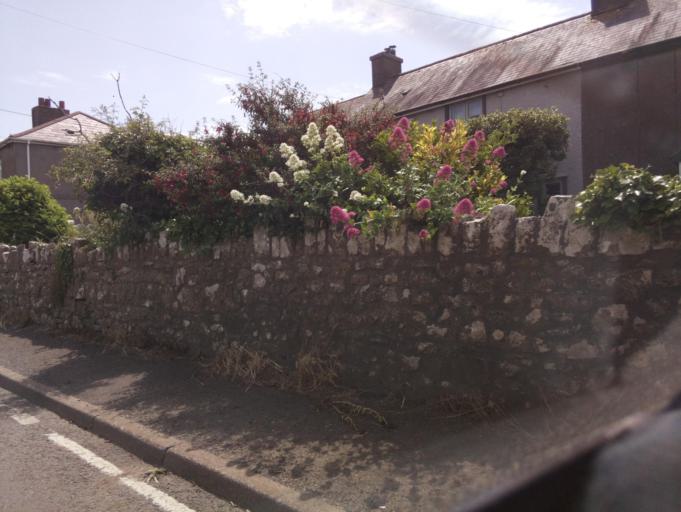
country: GB
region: Wales
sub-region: Bridgend county borough
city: Merthyr Mawr
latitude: 51.4556
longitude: -3.5881
